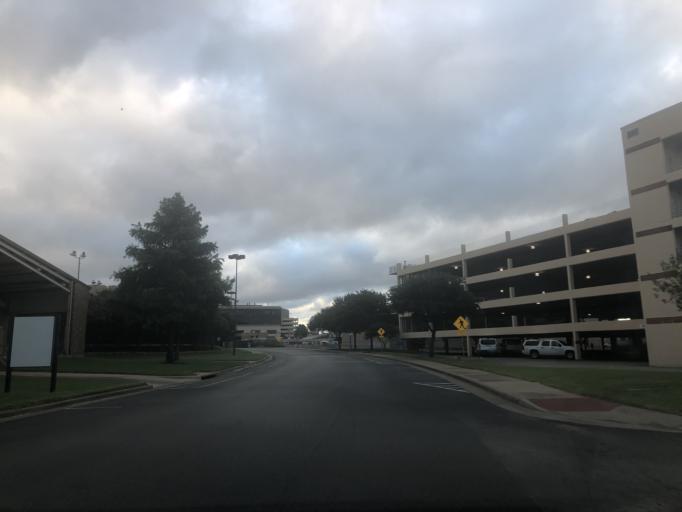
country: US
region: Texas
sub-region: Dallas County
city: Dallas
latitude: 32.8127
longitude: -96.8444
